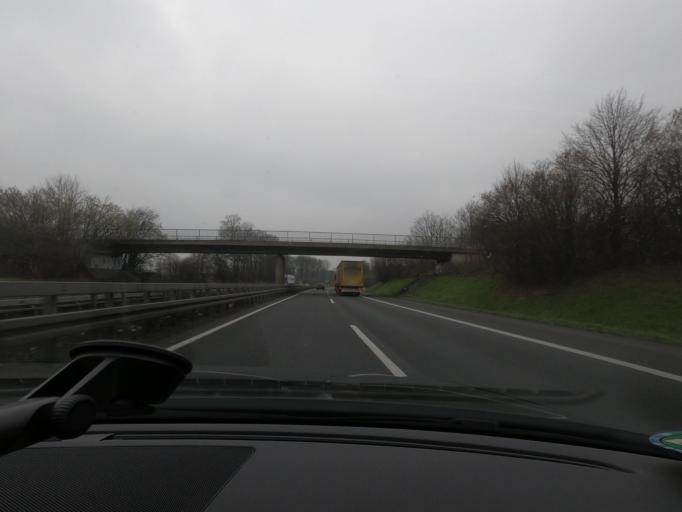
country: DE
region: North Rhine-Westphalia
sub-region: Regierungsbezirk Dusseldorf
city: Nettetal
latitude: 51.3098
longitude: 6.2271
